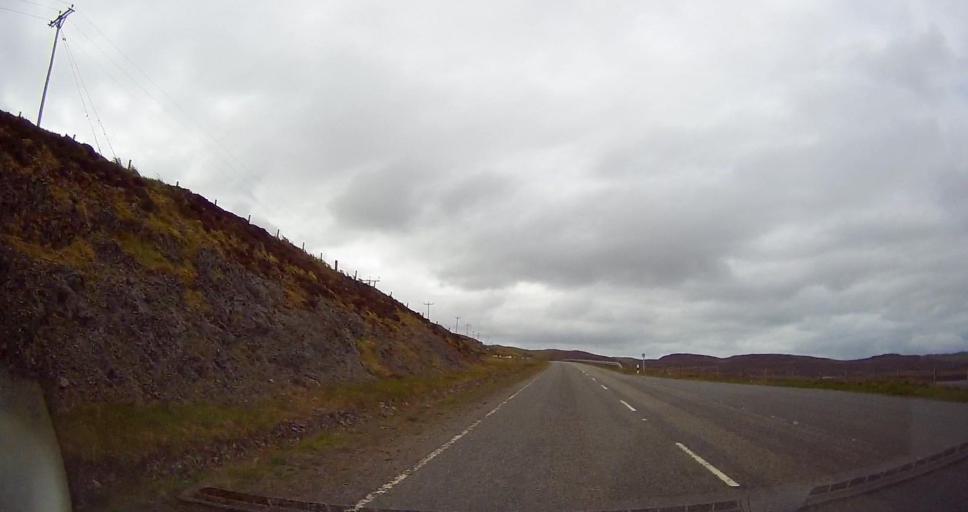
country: GB
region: Scotland
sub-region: Shetland Islands
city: Lerwick
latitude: 60.2571
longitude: -1.4708
